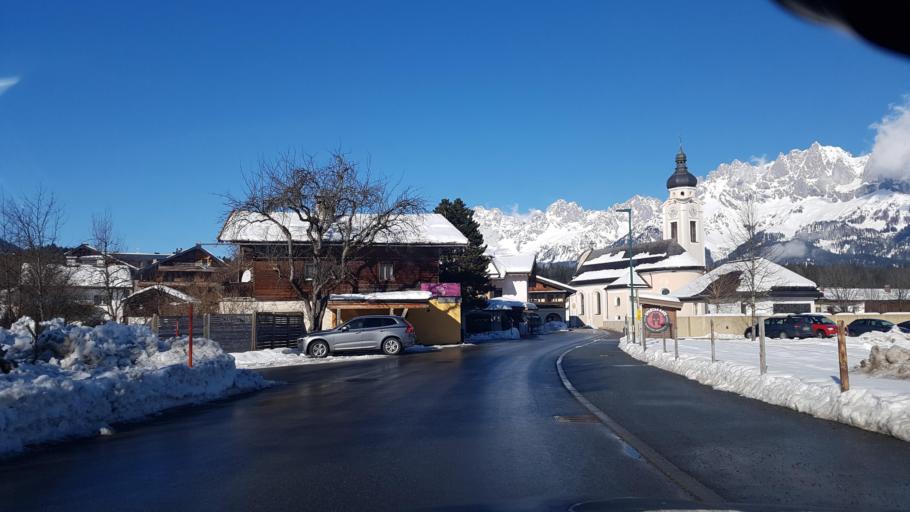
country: AT
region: Tyrol
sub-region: Politischer Bezirk Kitzbuhel
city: Oberndorf in Tirol
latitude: 47.4986
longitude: 12.3865
